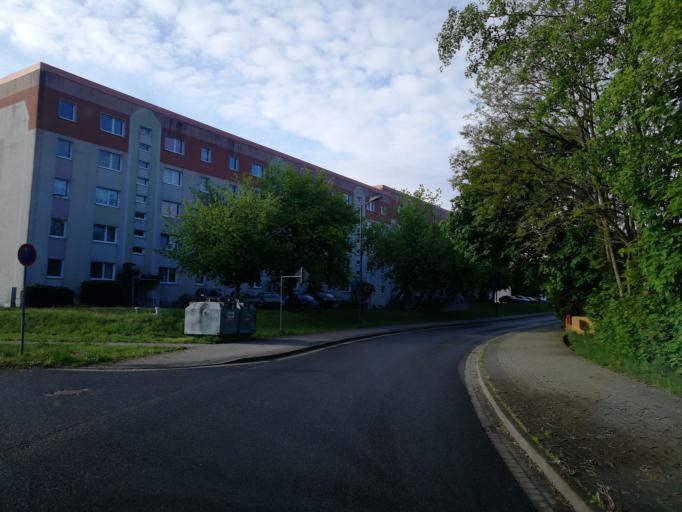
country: DE
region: Brandenburg
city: Lauchhammer
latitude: 51.5002
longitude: 13.7554
